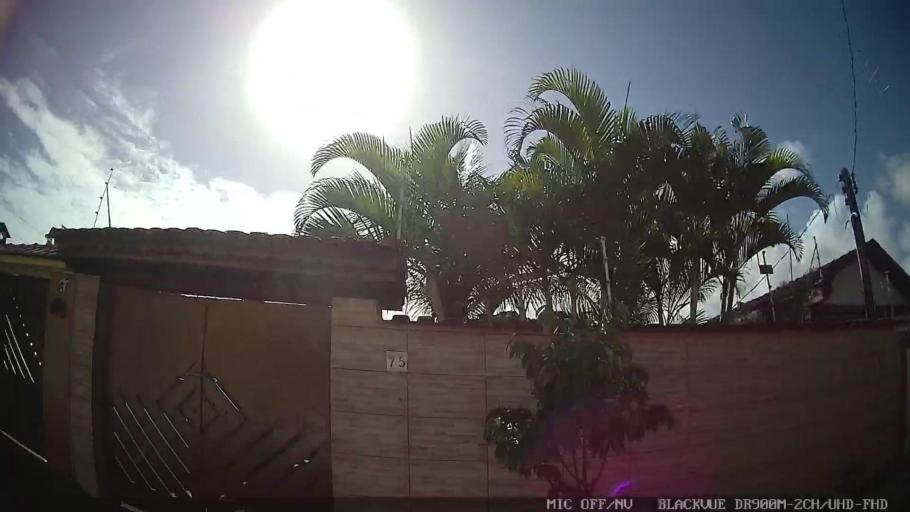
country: BR
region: Sao Paulo
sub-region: Itanhaem
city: Itanhaem
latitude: -24.1651
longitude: -46.7586
